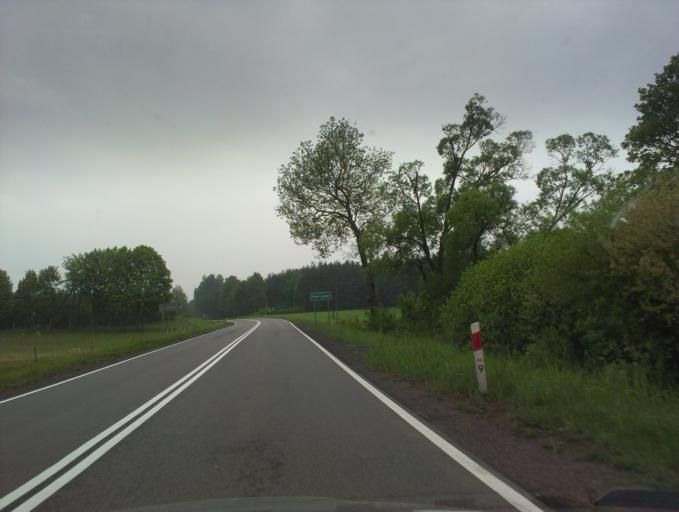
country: PL
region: West Pomeranian Voivodeship
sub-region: Powiat koszalinski
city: Bobolice
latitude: 53.9022
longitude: 16.6122
